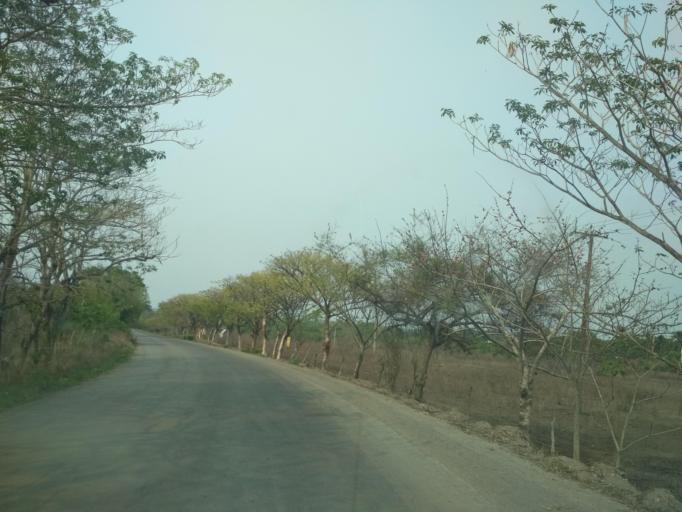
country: MX
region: Veracruz
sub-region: Veracruz
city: Delfino Victoria (Santa Fe)
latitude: 19.1952
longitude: -96.2916
